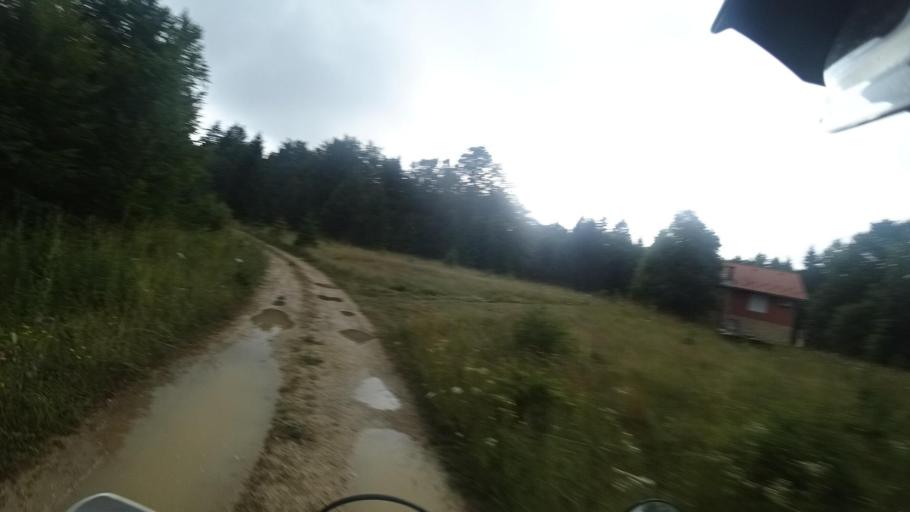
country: HR
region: Licko-Senjska
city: Jezerce
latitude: 44.8200
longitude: 15.6195
